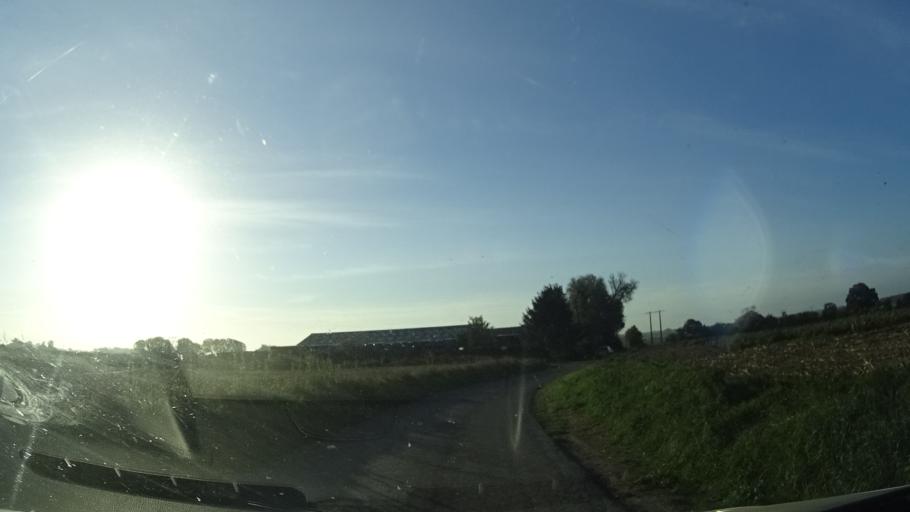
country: BE
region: Wallonia
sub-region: Province du Hainaut
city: Beaumont
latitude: 50.2382
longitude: 4.2720
